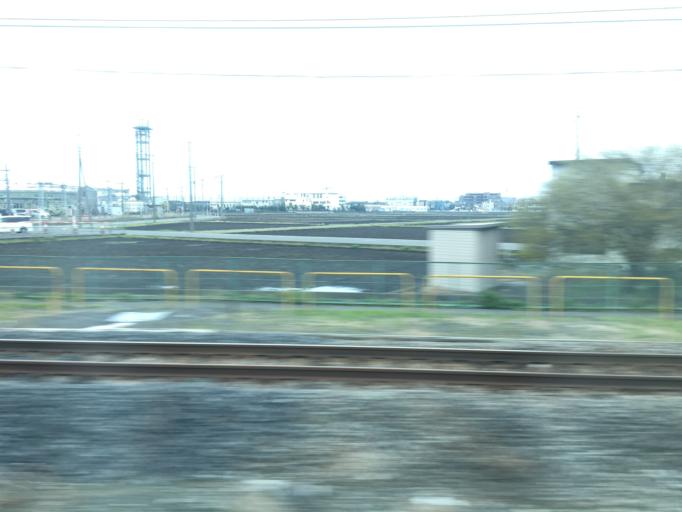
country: JP
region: Saitama
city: Kamifukuoka
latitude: 35.9036
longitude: 139.5254
